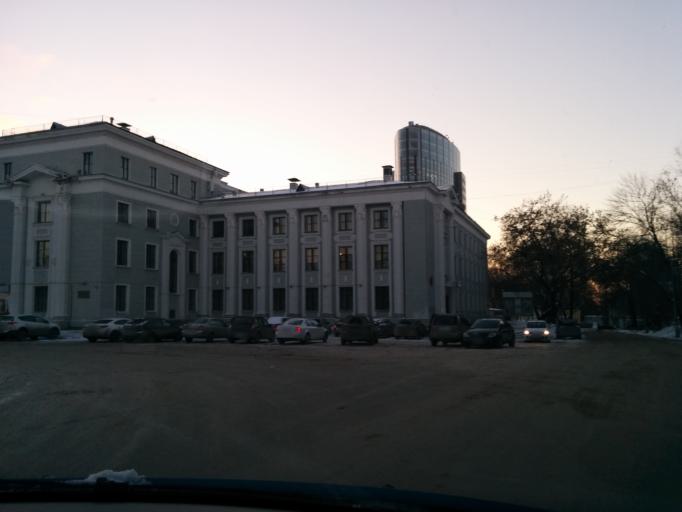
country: RU
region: Perm
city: Perm
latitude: 57.9914
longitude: 56.2514
